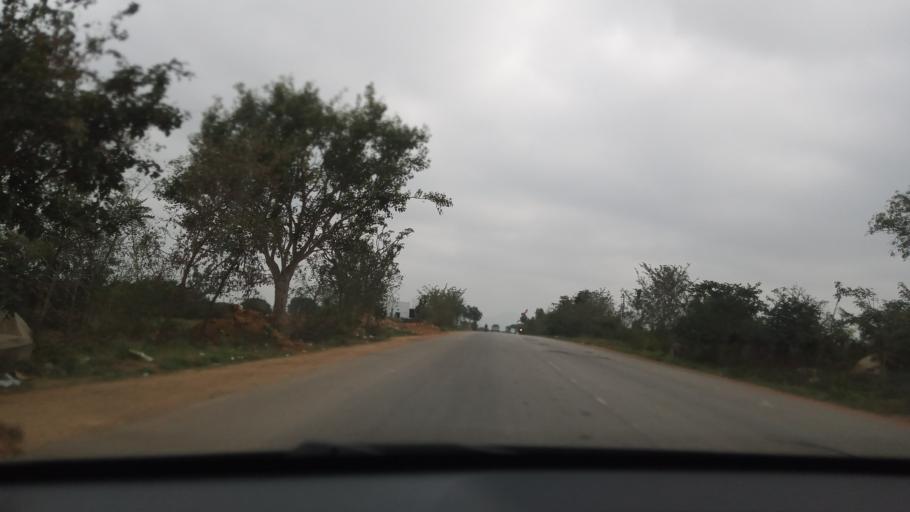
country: IN
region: Karnataka
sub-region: Chikkaballapur
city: Sidlaghatta
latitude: 13.2700
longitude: 77.9495
